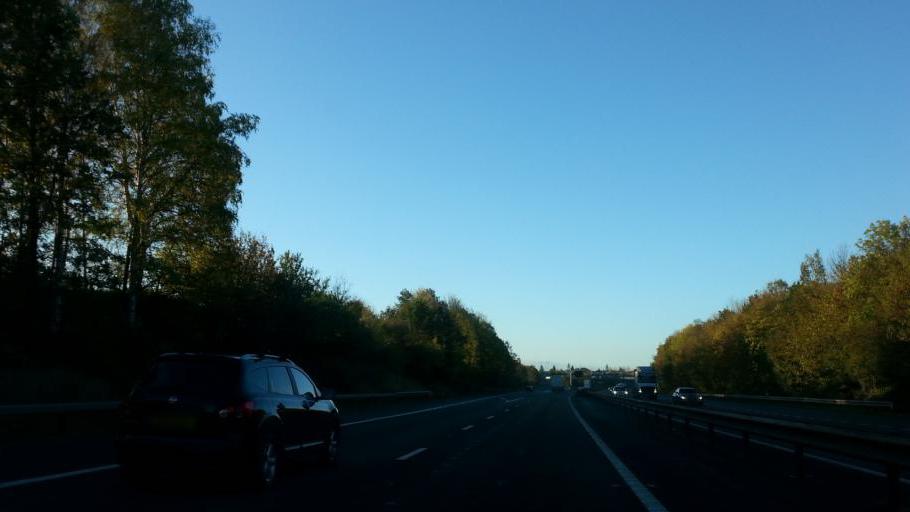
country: GB
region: England
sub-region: Staffordshire
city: Fazeley
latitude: 52.6086
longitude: -1.6368
